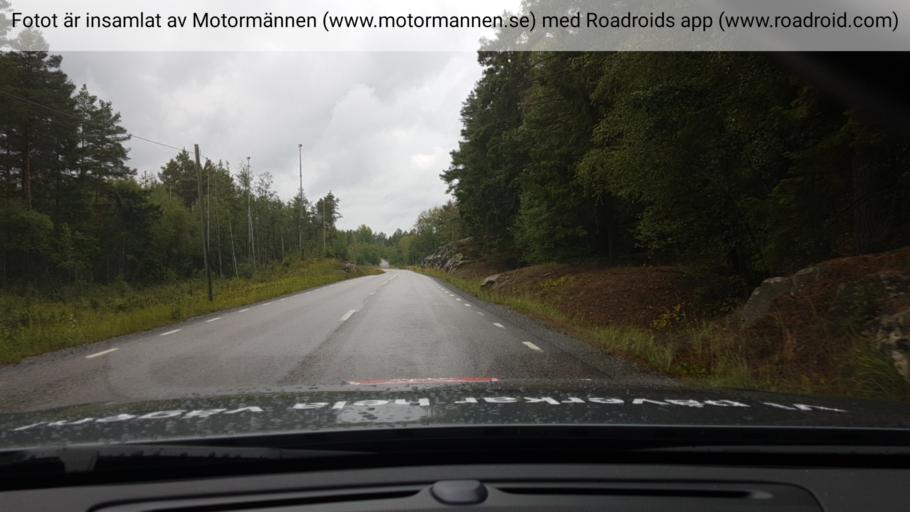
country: SE
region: Stockholm
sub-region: Botkyrka Kommun
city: Tullinge
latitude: 59.1869
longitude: 17.9285
